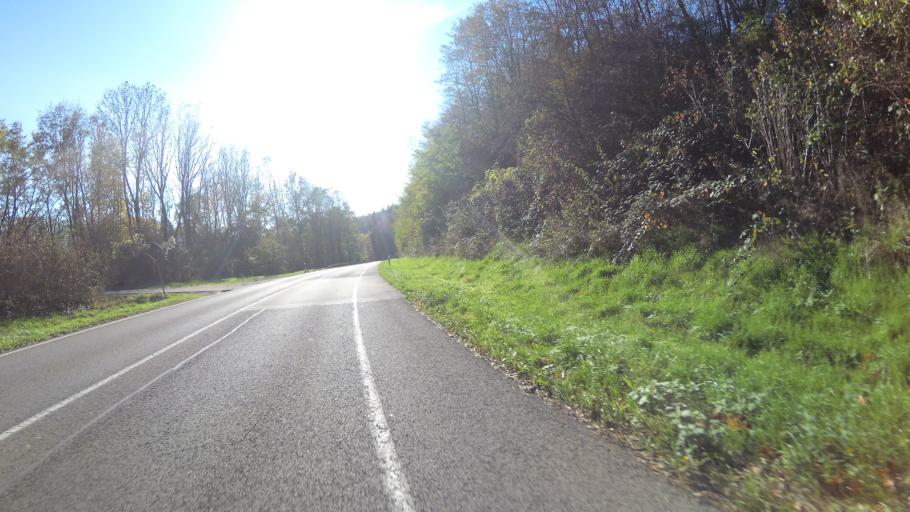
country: DE
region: Saarland
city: Losheim
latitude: 49.4765
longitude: 6.7504
